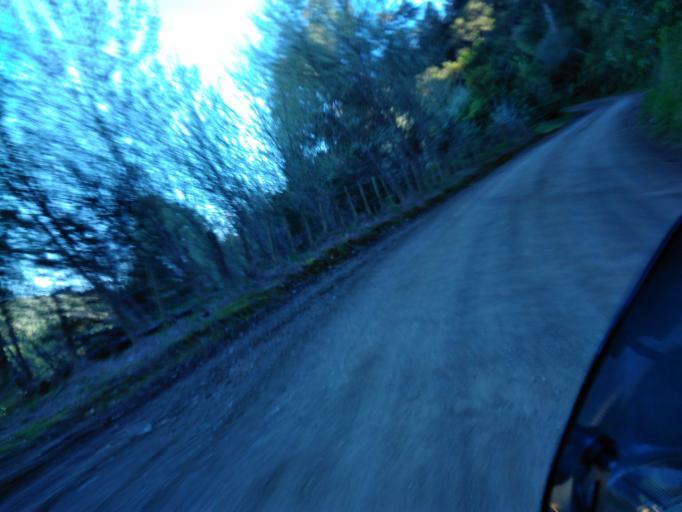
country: NZ
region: Gisborne
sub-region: Gisborne District
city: Gisborne
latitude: -38.4092
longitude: 177.6849
